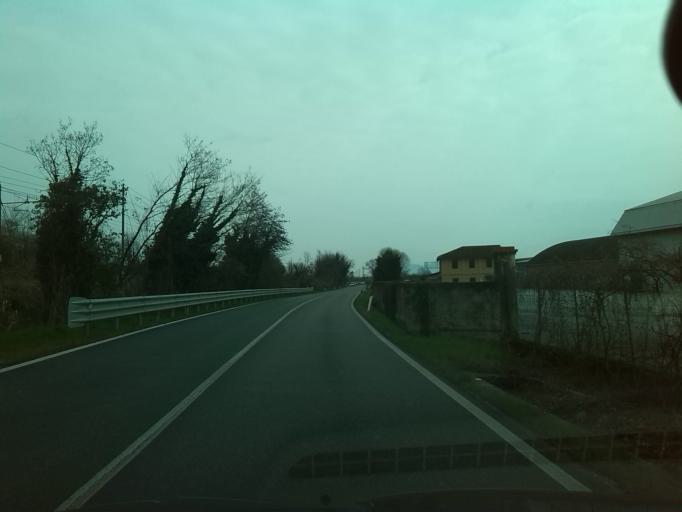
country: IT
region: Friuli Venezia Giulia
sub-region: Provincia di Gorizia
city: Moraro
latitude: 45.9455
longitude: 13.4881
